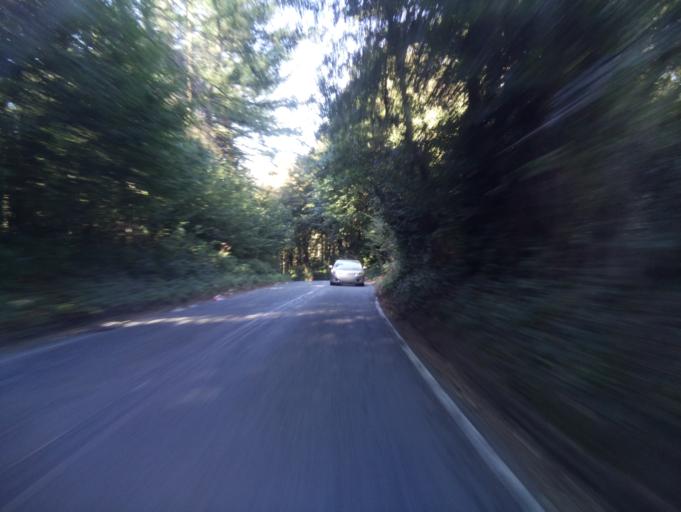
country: GB
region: Wales
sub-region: Newport
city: Newport
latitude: 51.6032
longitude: -3.0470
